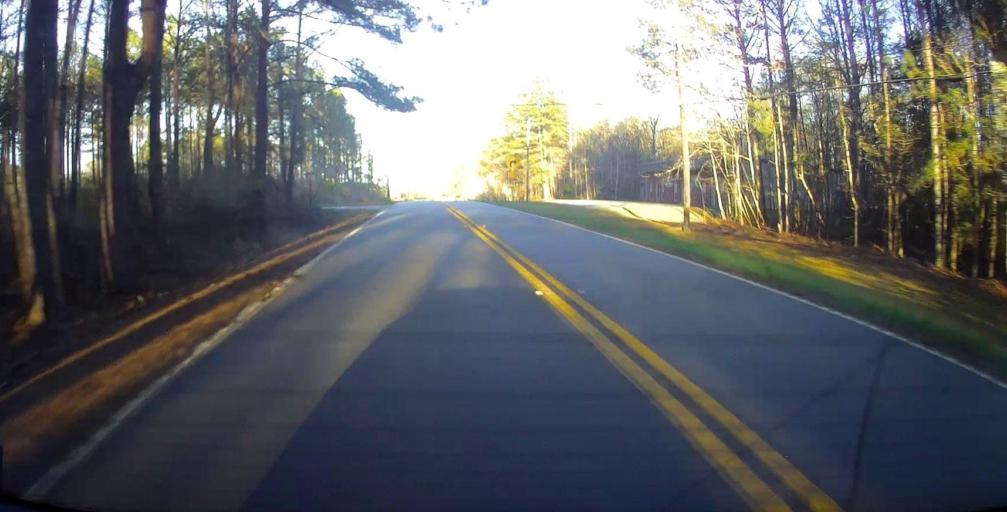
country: US
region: Georgia
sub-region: Harris County
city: Hamilton
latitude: 32.6567
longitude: -84.8518
